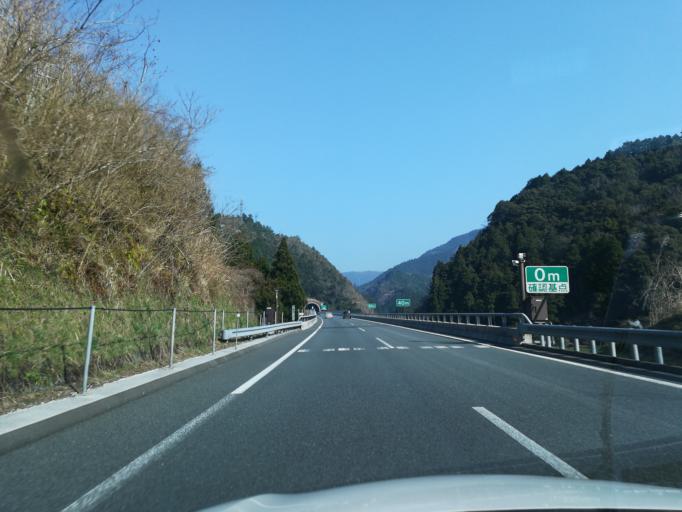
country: JP
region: Ehime
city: Kawanoecho
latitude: 33.8228
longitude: 133.6627
